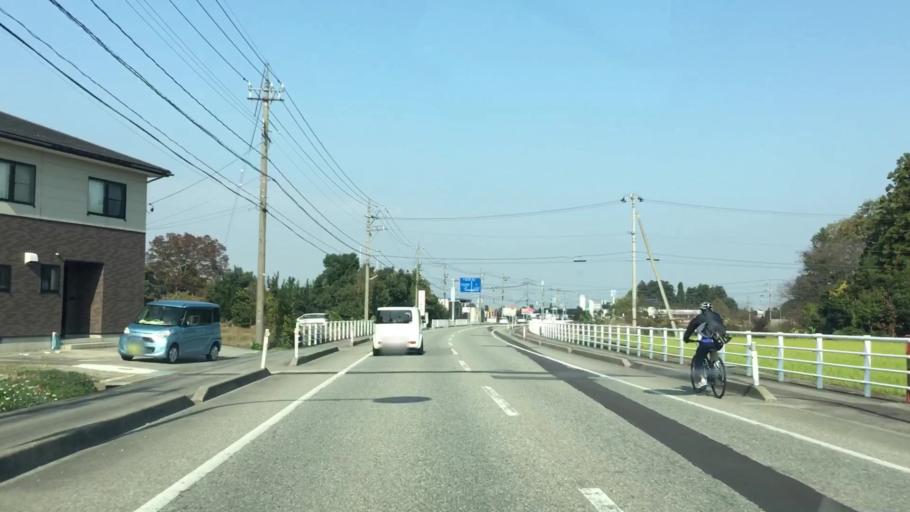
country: JP
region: Toyama
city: Yatsuomachi-higashikumisaka
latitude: 36.5954
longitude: 137.1912
